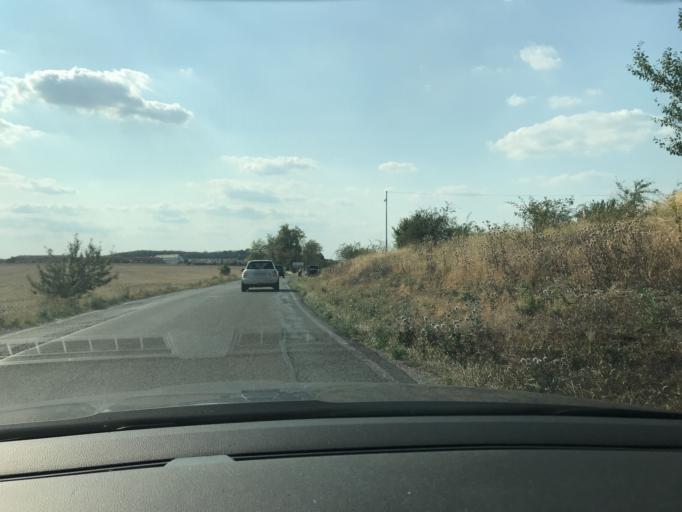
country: CZ
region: Central Bohemia
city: Velke Prilepy
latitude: 50.1545
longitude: 14.3313
